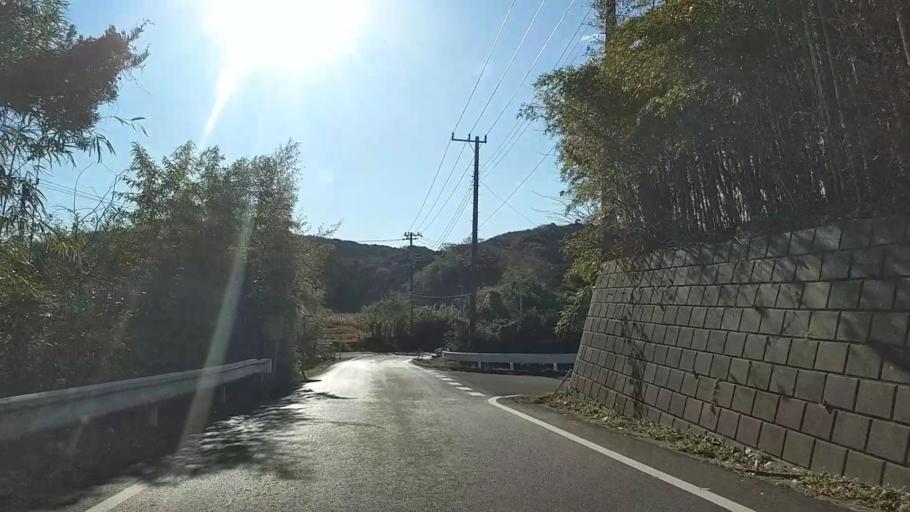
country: JP
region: Chiba
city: Futtsu
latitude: 35.2329
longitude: 139.8767
